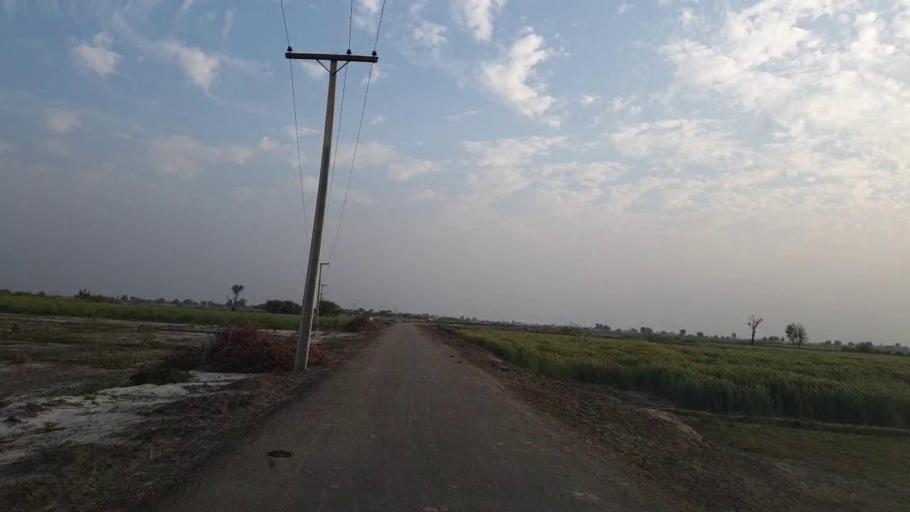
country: PK
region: Sindh
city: Pithoro
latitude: 25.5878
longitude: 69.3100
